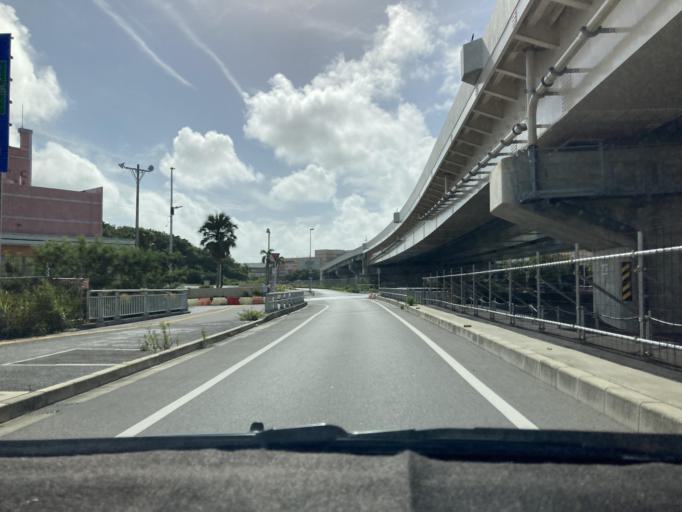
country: JP
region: Okinawa
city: Naha-shi
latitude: 26.2036
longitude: 127.7351
